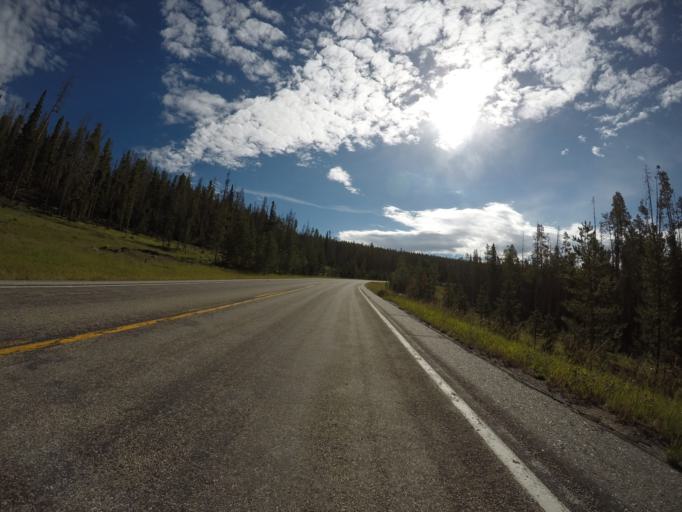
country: US
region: Wyoming
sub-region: Carbon County
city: Saratoga
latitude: 41.3294
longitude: -106.4799
